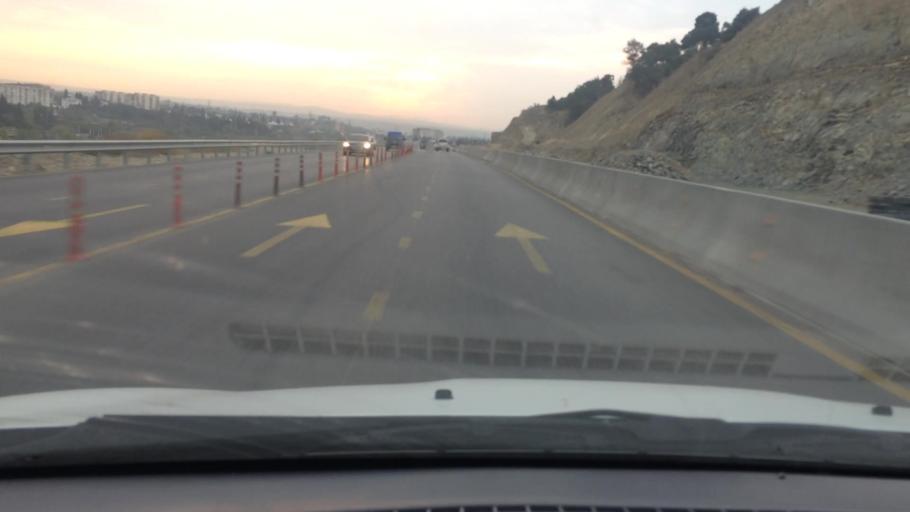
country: GE
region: T'bilisi
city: Tbilisi
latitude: 41.6628
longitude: 44.8782
